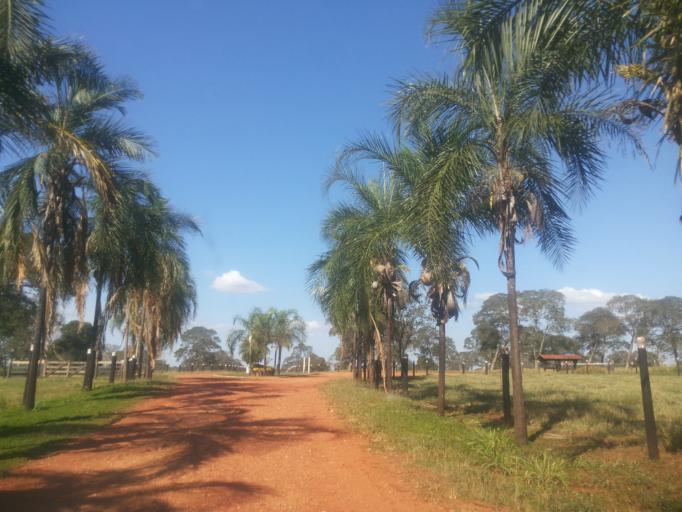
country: BR
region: Minas Gerais
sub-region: Santa Vitoria
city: Santa Vitoria
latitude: -19.0047
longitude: -50.4270
